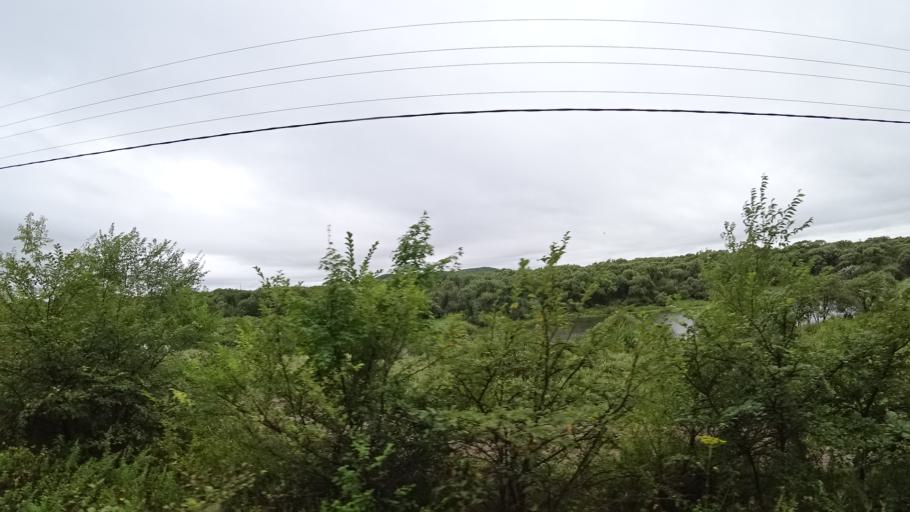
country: RU
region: Primorskiy
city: Monastyrishche
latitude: 44.2672
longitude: 132.4038
